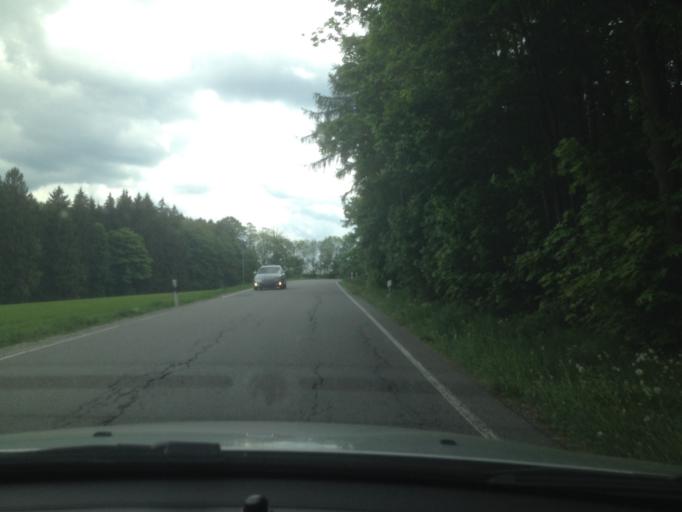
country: DE
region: Saxony
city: Zwonitz
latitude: 50.6469
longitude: 12.7812
